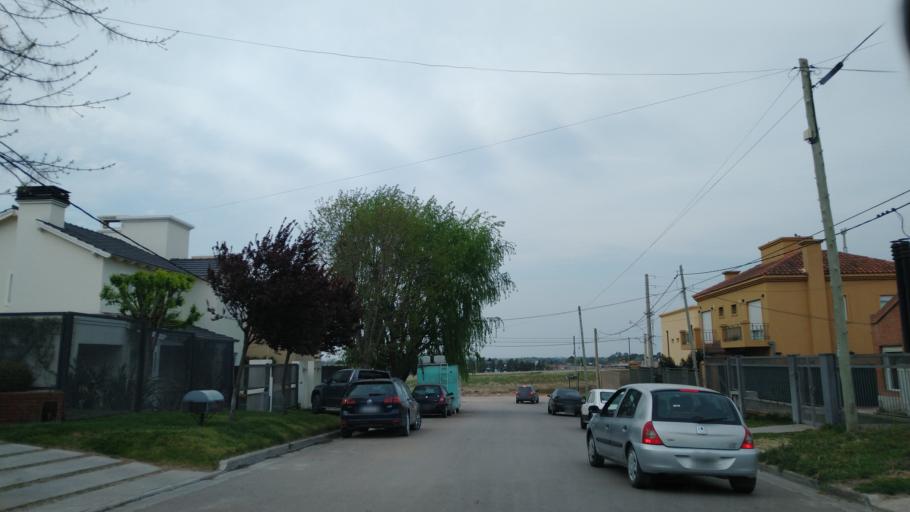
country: AR
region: Buenos Aires
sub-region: Partido de Bahia Blanca
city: Bahia Blanca
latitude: -38.6971
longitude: -62.2353
